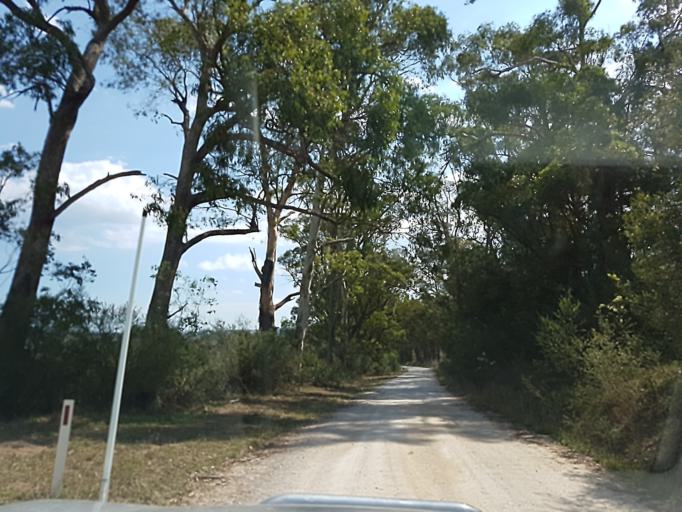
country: AU
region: Victoria
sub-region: East Gippsland
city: Lakes Entrance
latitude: -37.4975
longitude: 148.2263
